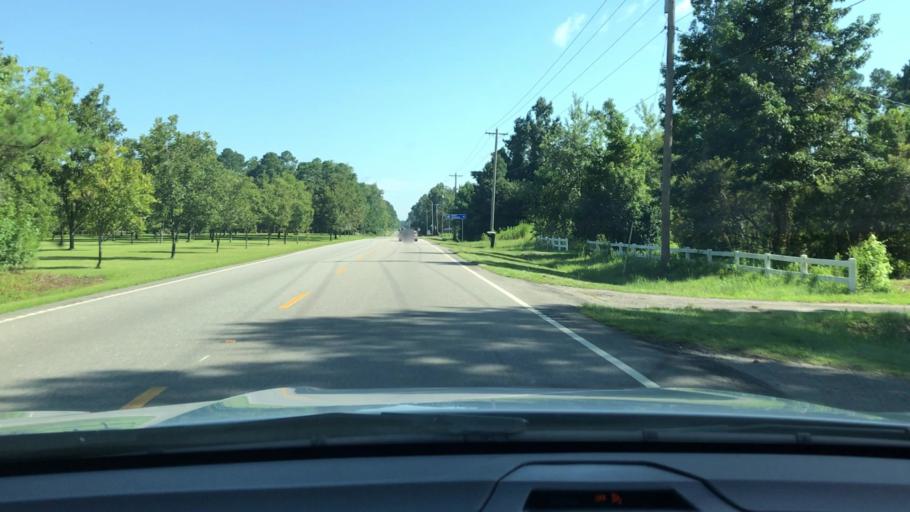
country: US
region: South Carolina
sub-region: Horry County
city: Conway
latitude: 33.7464
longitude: -79.0789
